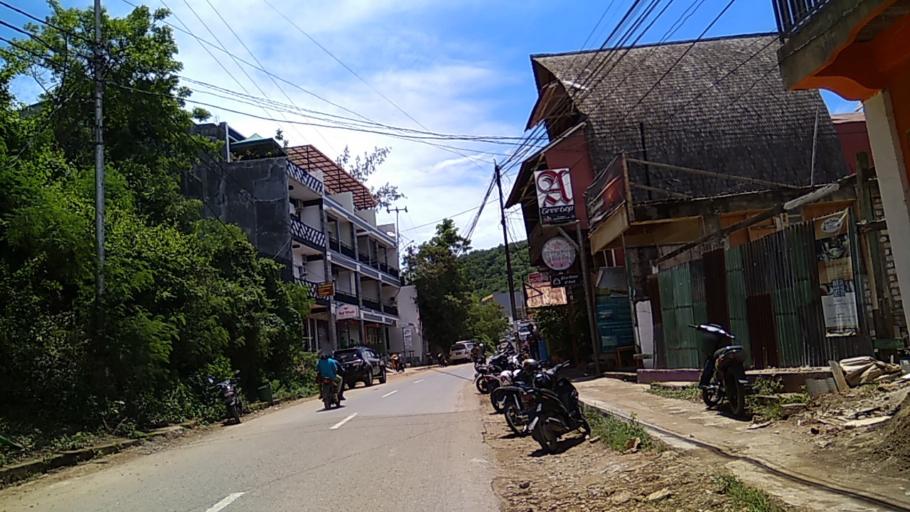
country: ID
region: East Nusa Tenggara
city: Cempa
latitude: -8.4951
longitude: 119.8787
